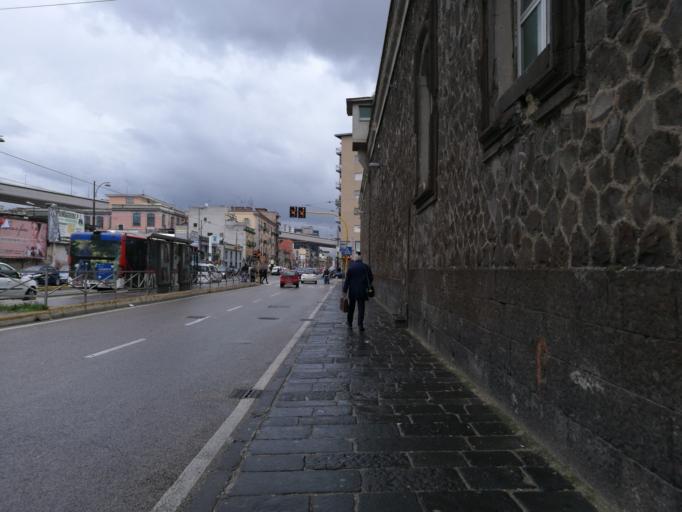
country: IT
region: Campania
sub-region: Provincia di Napoli
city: Napoli
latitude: 40.8614
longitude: 14.2803
